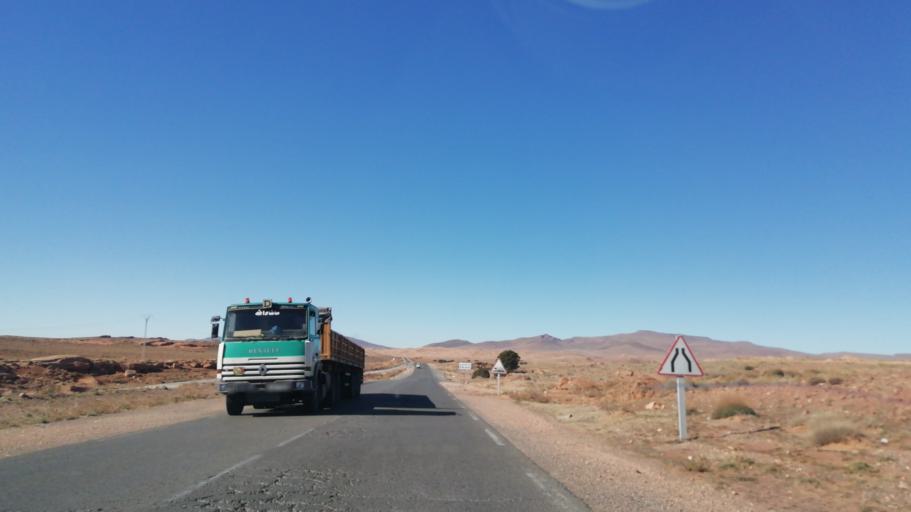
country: DZ
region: El Bayadh
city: El Bayadh
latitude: 33.6140
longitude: 1.2184
